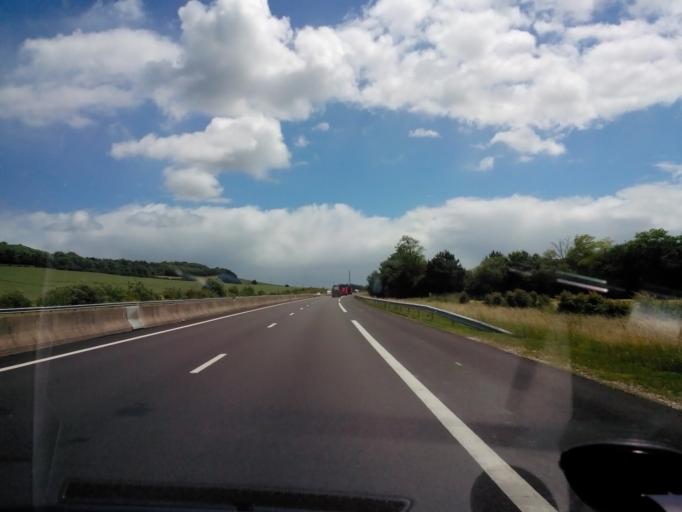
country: FR
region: Champagne-Ardenne
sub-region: Departement de la Haute-Marne
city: Nogent-le-Bas
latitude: 47.9570
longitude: 5.4102
